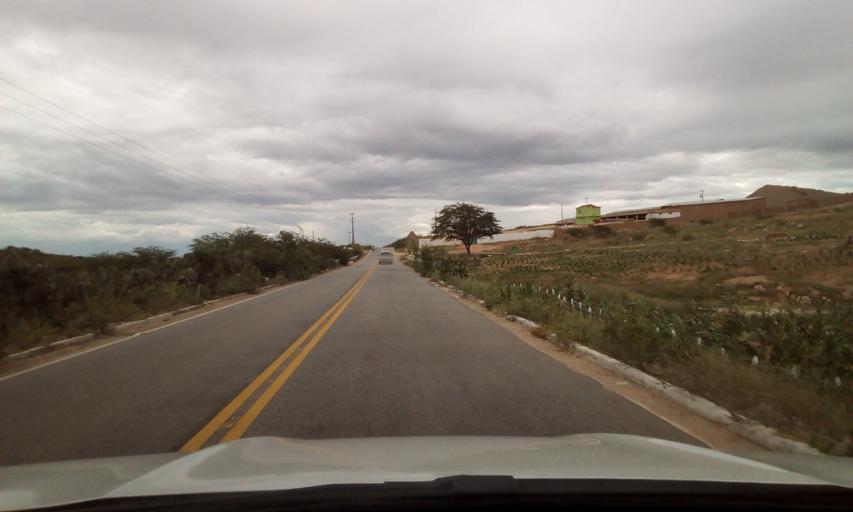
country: BR
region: Paraiba
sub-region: Picui
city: Picui
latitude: -6.5471
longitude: -36.2984
